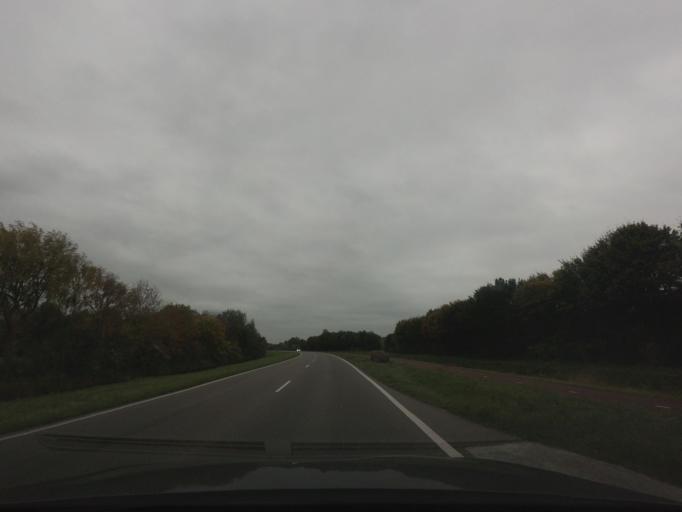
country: NL
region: North Holland
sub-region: Gemeente Alkmaar
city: Alkmaar
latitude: 52.6602
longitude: 4.7434
